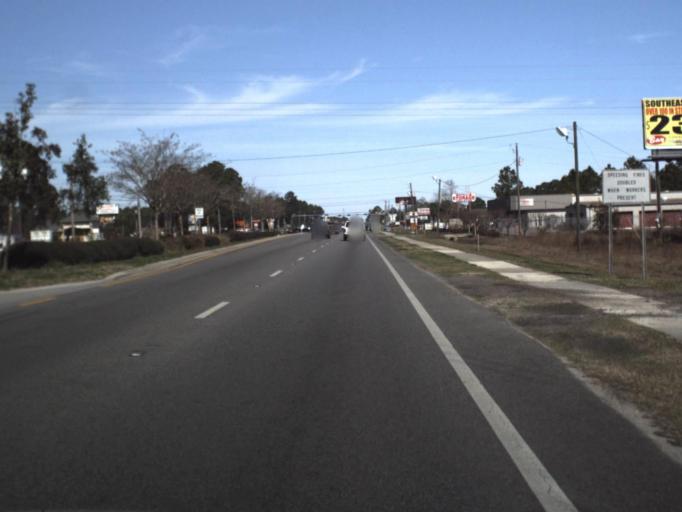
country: US
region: Florida
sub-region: Bay County
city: Hiland Park
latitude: 30.2077
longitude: -85.6495
